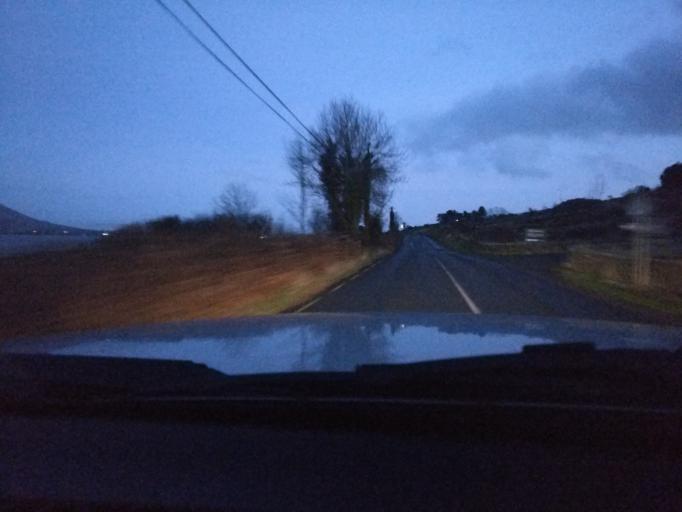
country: GB
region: Northern Ireland
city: Rostrevor
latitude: 54.0669
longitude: -6.2213
